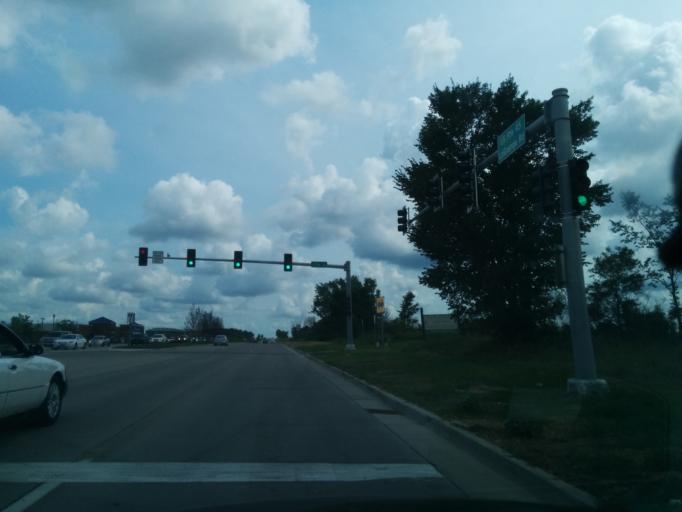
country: US
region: Illinois
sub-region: Cook County
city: Orland Hills
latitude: 41.5798
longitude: -87.8522
